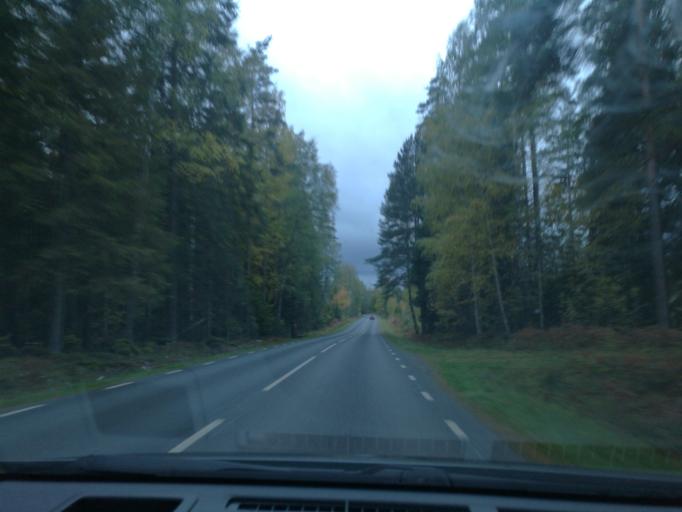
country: SE
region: Soedermanland
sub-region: Vingakers Kommun
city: Vingaker
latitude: 59.0862
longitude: 15.9093
